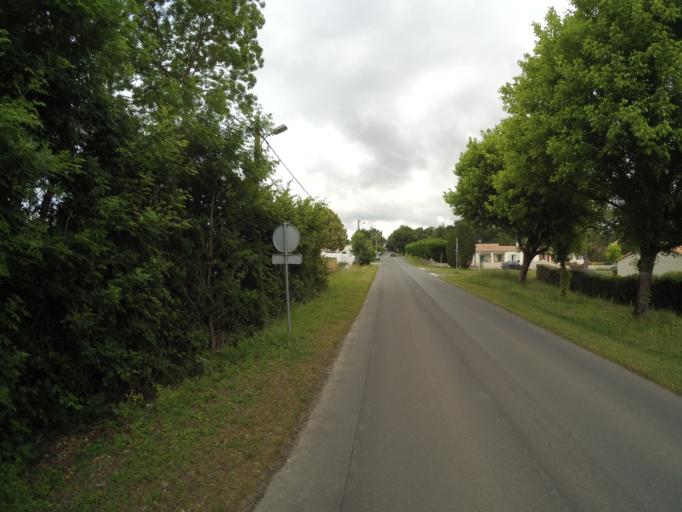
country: FR
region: Poitou-Charentes
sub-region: Departement de la Charente-Maritime
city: Breuil-Magne
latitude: 45.9624
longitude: -0.9699
